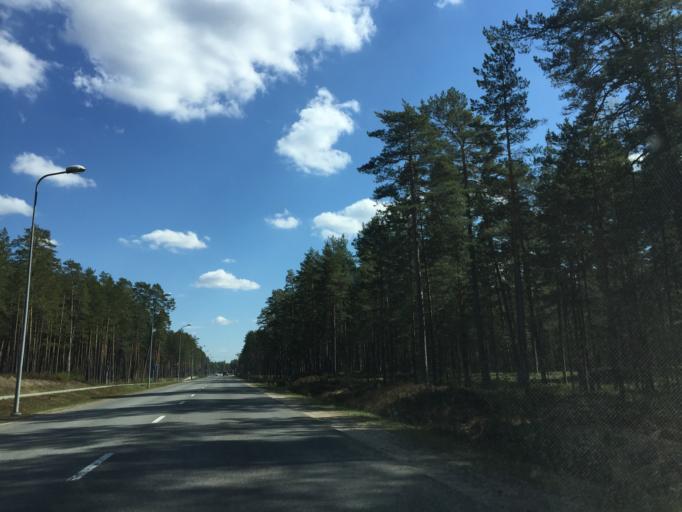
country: LV
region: Saulkrastu
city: Saulkrasti
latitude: 57.2505
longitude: 24.4112
